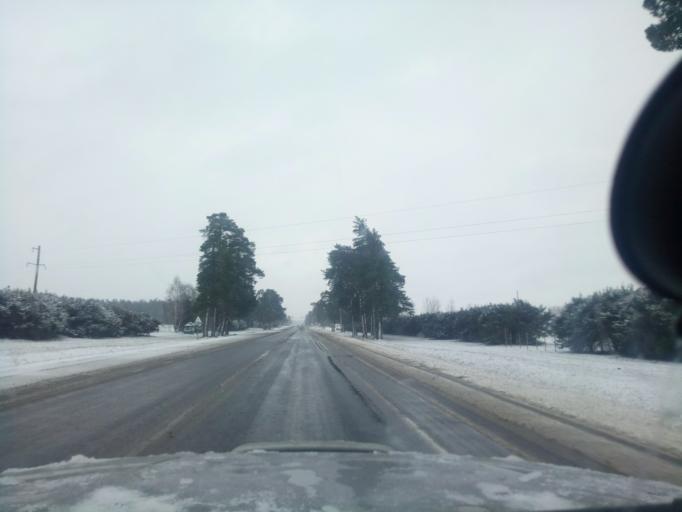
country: BY
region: Minsk
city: Nyasvizh
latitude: 53.2496
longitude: 26.6220
